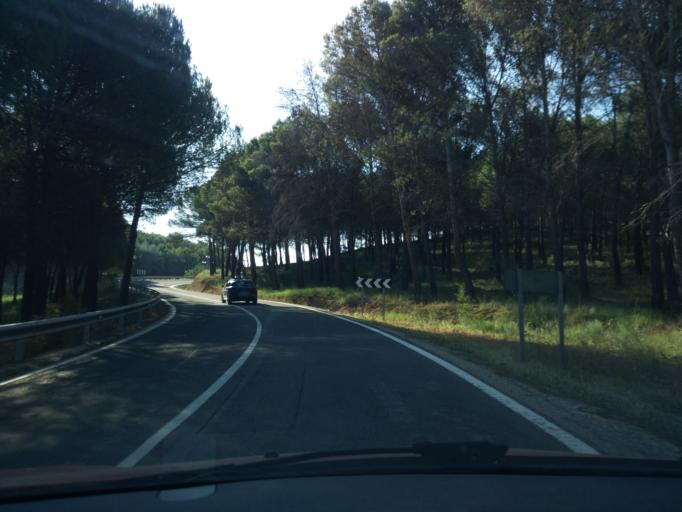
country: ES
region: Madrid
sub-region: Provincia de Madrid
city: Corpa
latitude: 40.3990
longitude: -3.2699
